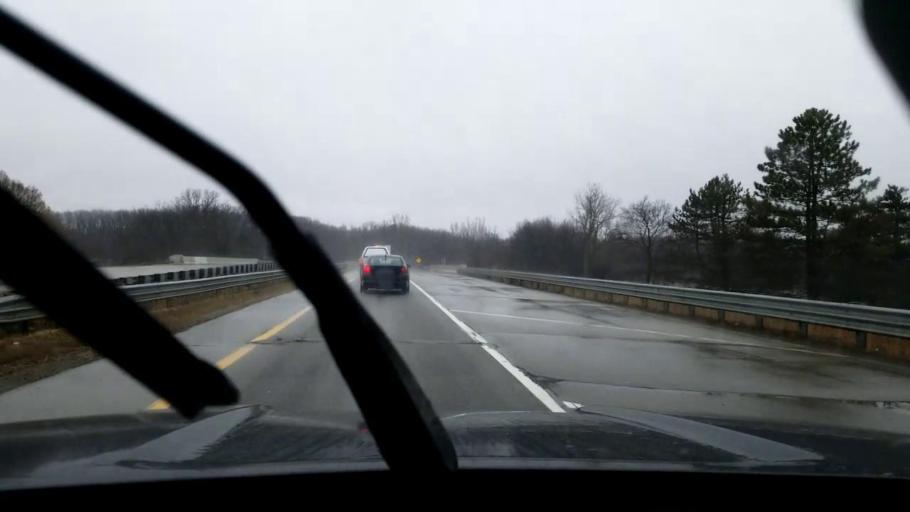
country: US
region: Michigan
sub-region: Jackson County
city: Jackson
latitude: 42.2759
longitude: -84.3586
